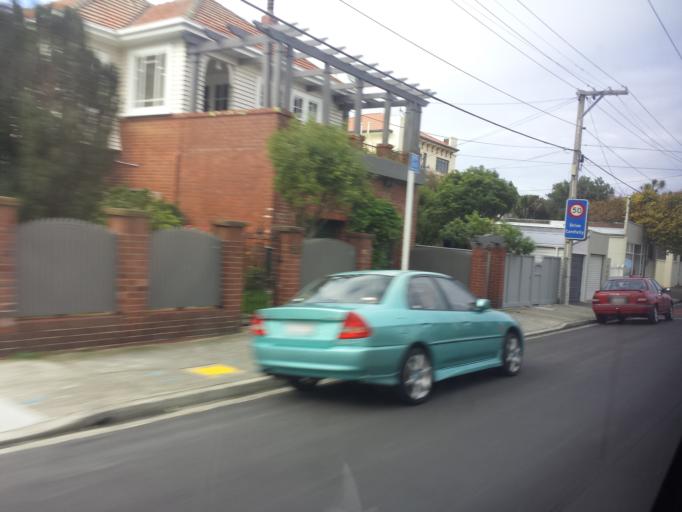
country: NZ
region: Wellington
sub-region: Wellington City
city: Wellington
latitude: -41.3053
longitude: 174.7937
